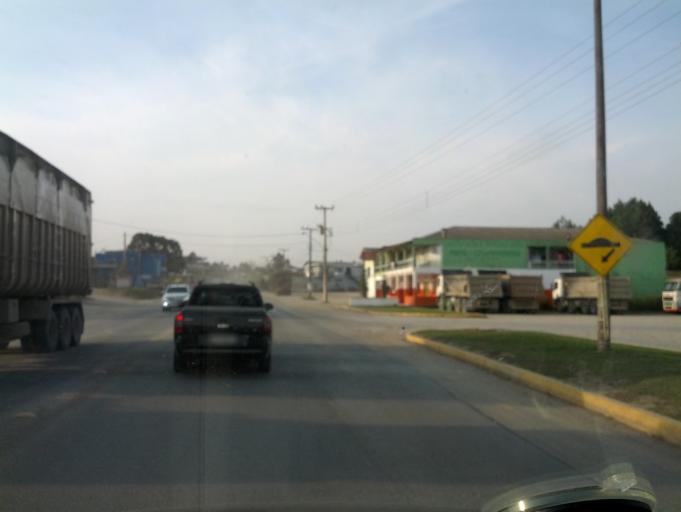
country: BR
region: Santa Catarina
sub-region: Otacilio Costa
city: Otacilio Costa
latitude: -27.4933
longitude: -50.1204
